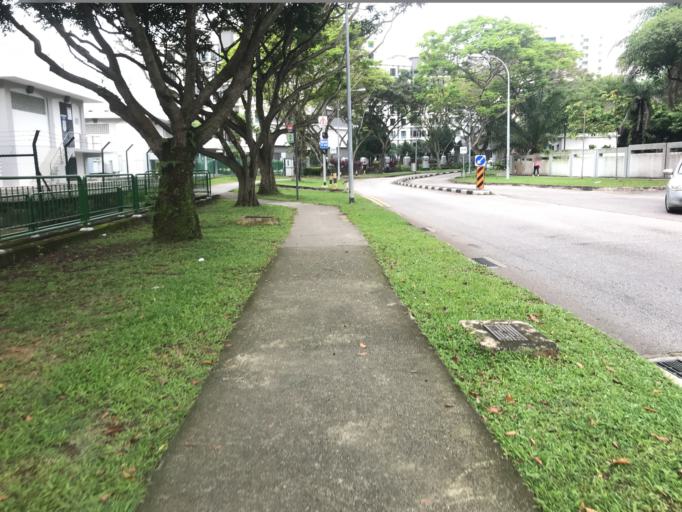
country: SG
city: Singapore
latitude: 1.3493
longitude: 103.8658
